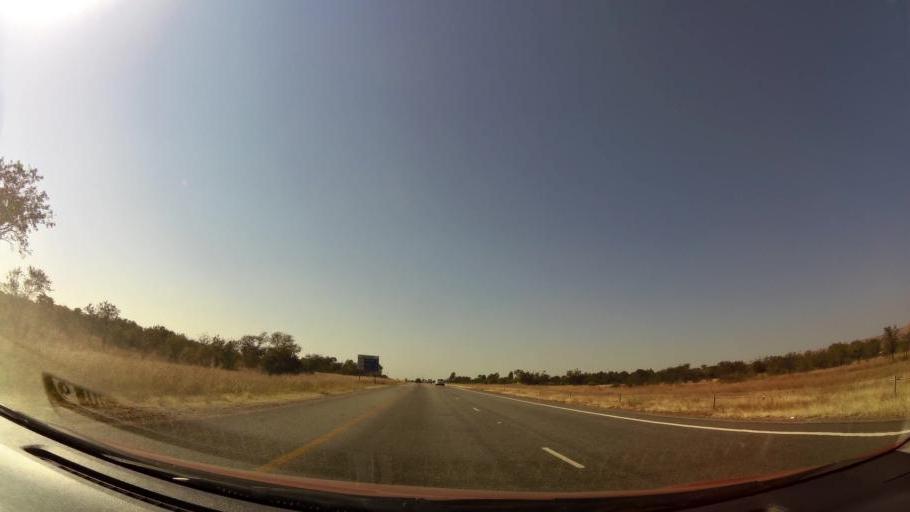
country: ZA
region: North-West
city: Ga-Rankuwa
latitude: -25.6579
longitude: 28.0701
